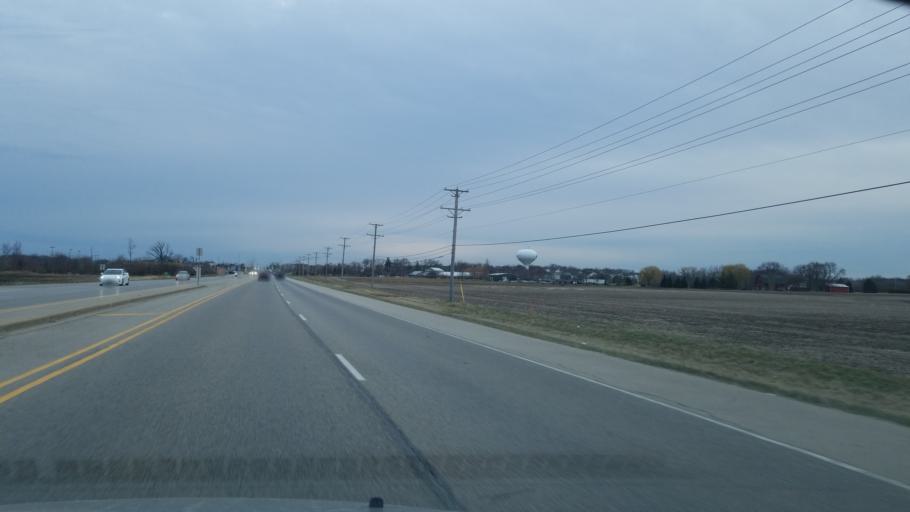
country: US
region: Illinois
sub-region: Kane County
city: Gilberts
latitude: 42.1328
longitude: -88.3356
